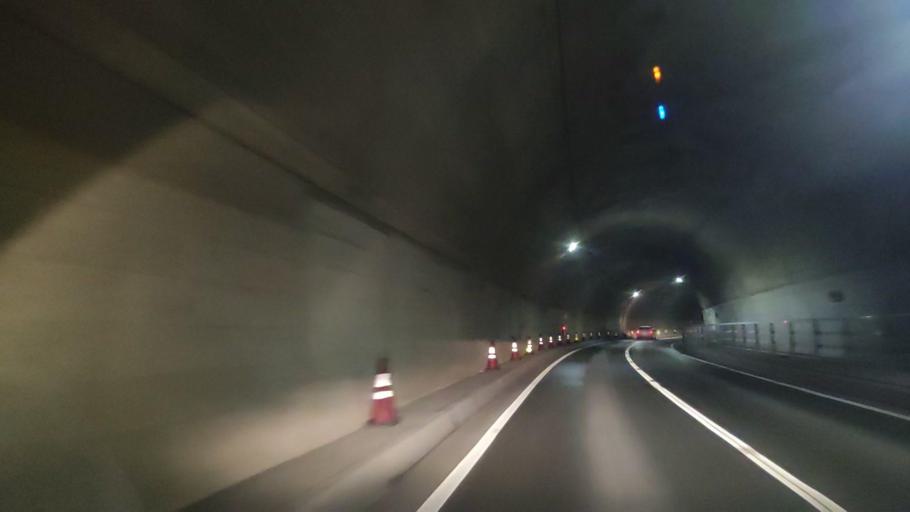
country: JP
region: Hokkaido
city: Sapporo
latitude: 42.9868
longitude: 141.1633
